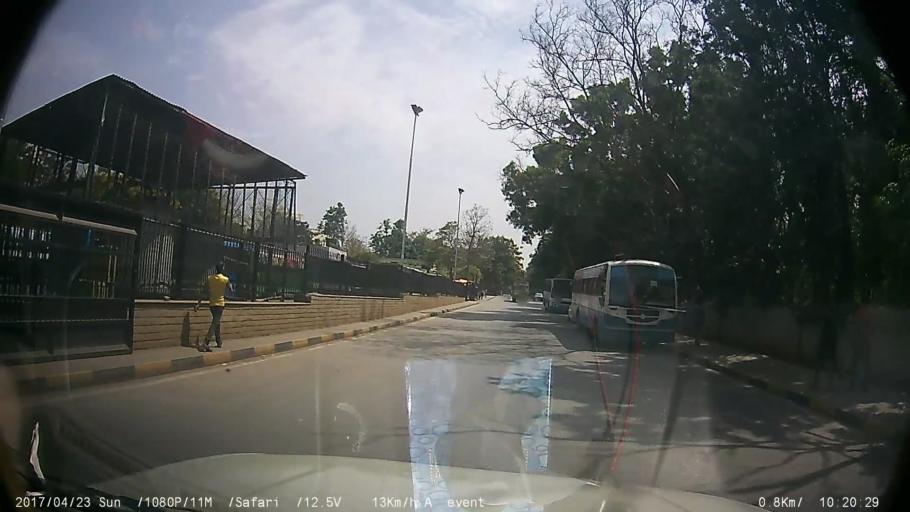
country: IN
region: Karnataka
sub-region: Bangalore Urban
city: Anekal
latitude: 12.8355
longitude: 77.6572
